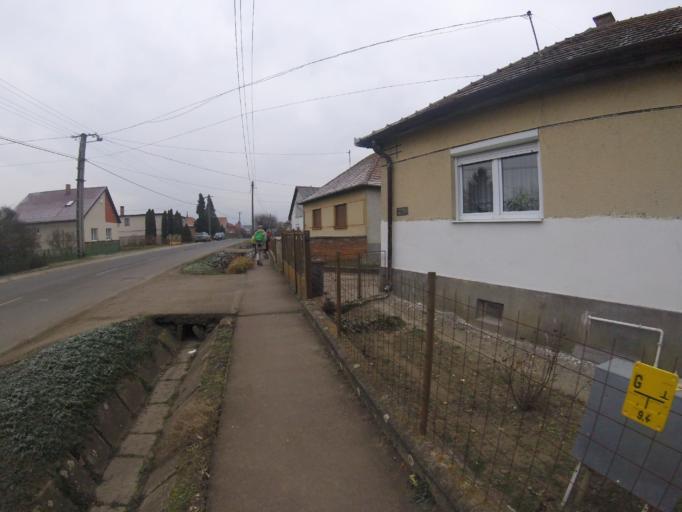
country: HU
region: Nograd
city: Paszto
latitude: 47.9466
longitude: 19.7000
